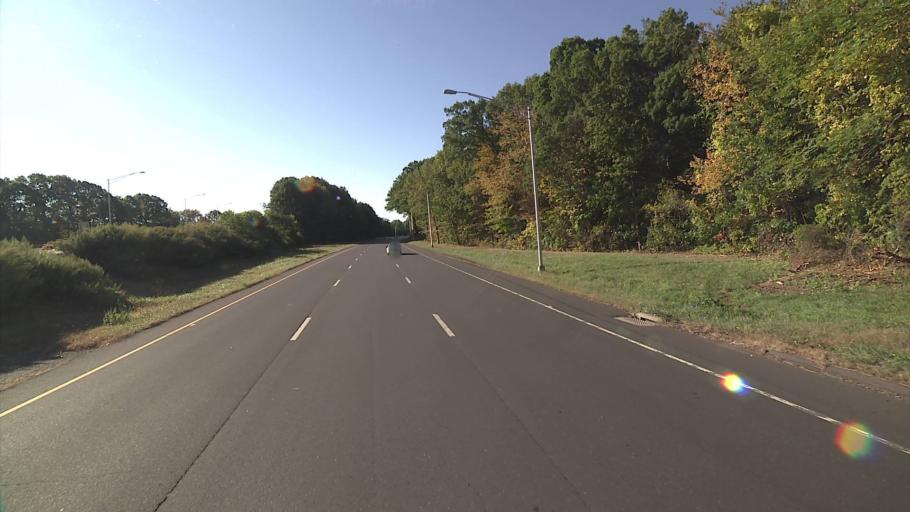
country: US
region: Connecticut
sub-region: New Haven County
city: Meriden
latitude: 41.5376
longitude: -72.7699
